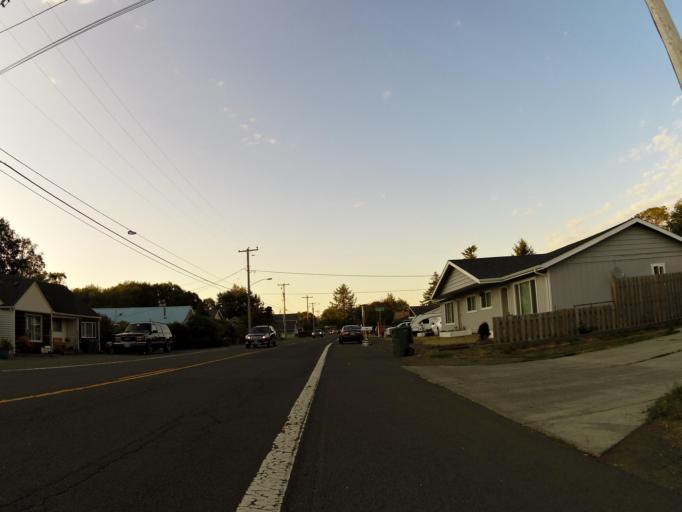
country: US
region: Oregon
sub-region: Clatsop County
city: Warrenton
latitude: 46.1534
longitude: -123.9278
